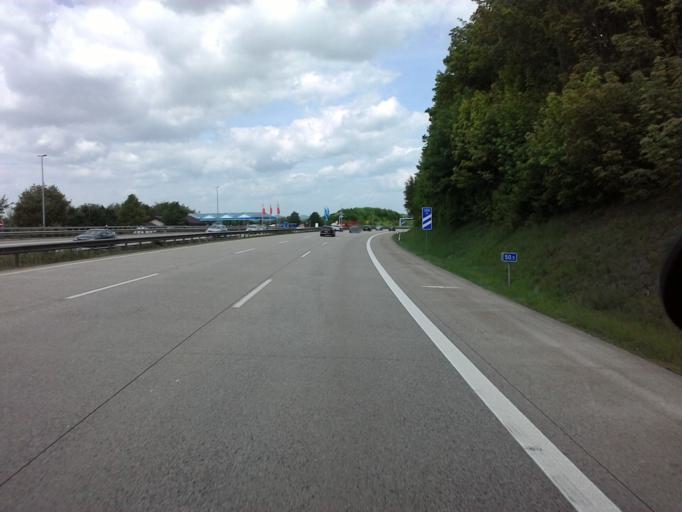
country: DE
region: Rheinland-Pfalz
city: Breitscheid
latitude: 50.5989
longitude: 7.4354
